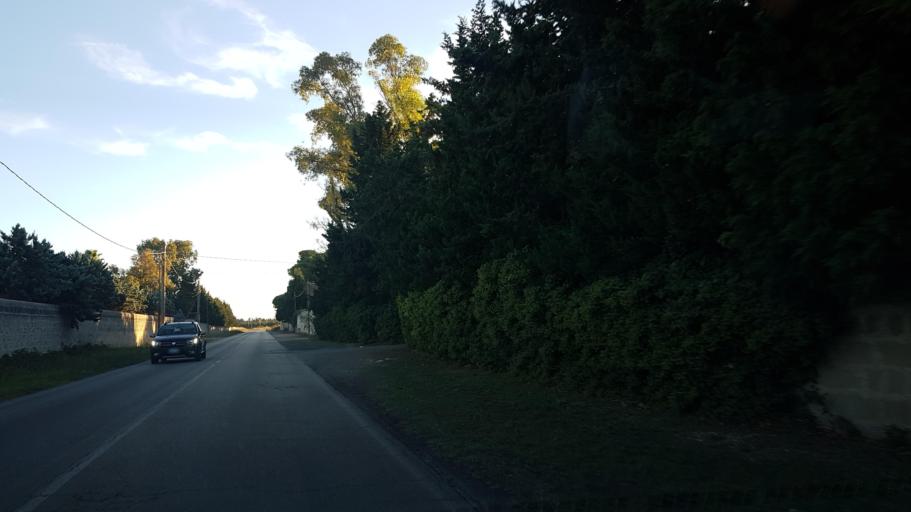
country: IT
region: Apulia
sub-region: Provincia di Lecce
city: Lecce
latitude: 40.3920
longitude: 18.1924
